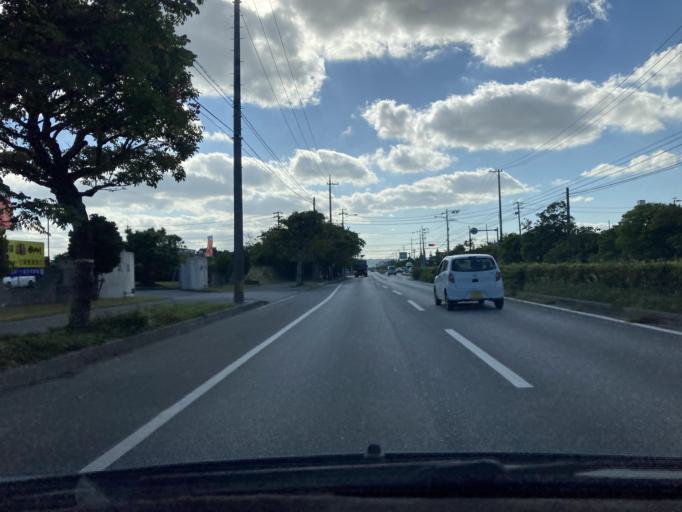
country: JP
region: Okinawa
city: Katsuren-haebaru
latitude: 26.3362
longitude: 127.8508
